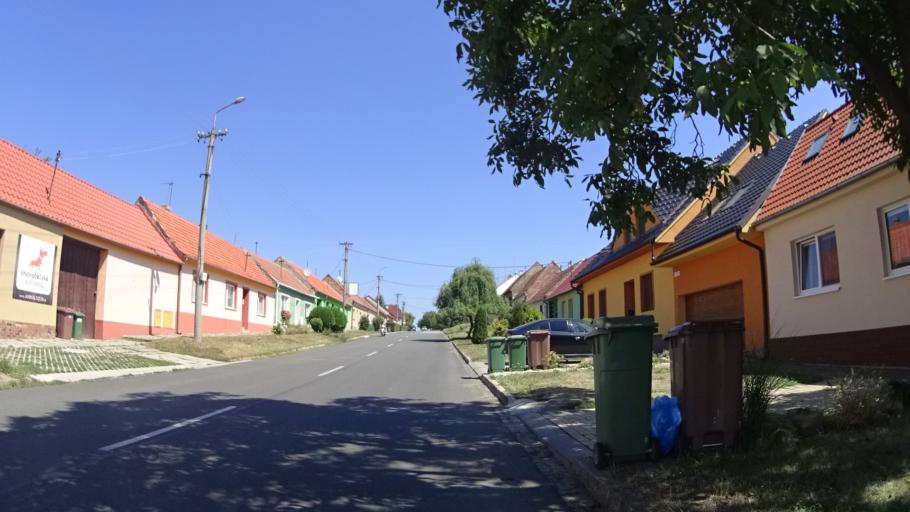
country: SK
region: Trnavsky
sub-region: Okres Skalica
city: Skalica
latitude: 48.8490
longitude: 17.2360
